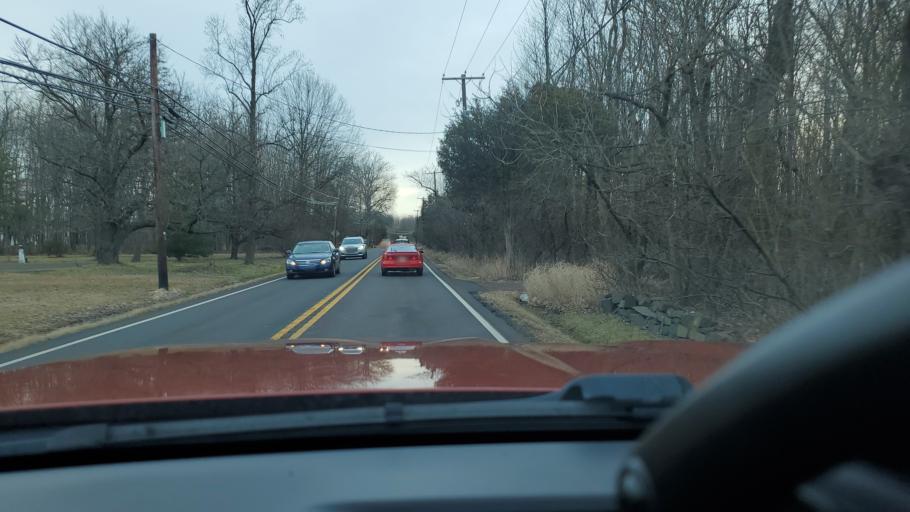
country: US
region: Pennsylvania
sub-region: Bucks County
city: Sellersville
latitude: 40.3598
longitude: -75.3465
